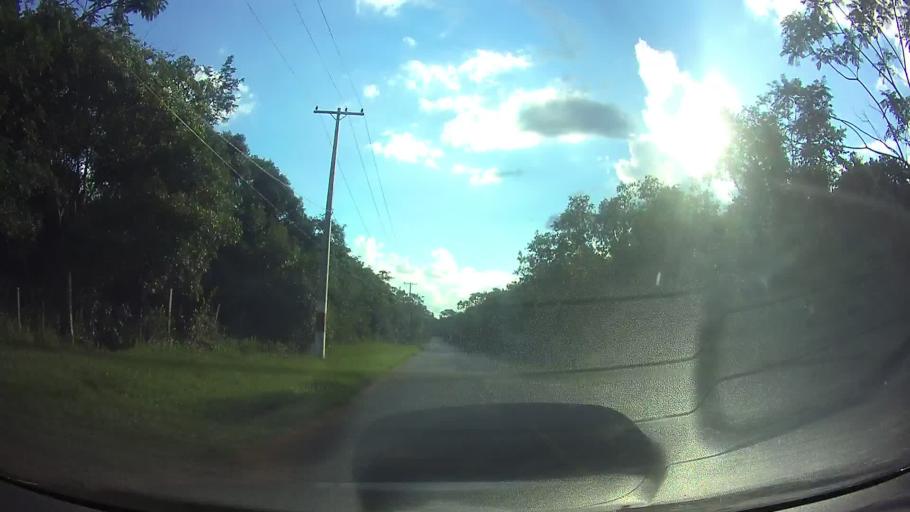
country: PY
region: Central
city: Aregua
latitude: -25.2701
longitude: -57.4279
